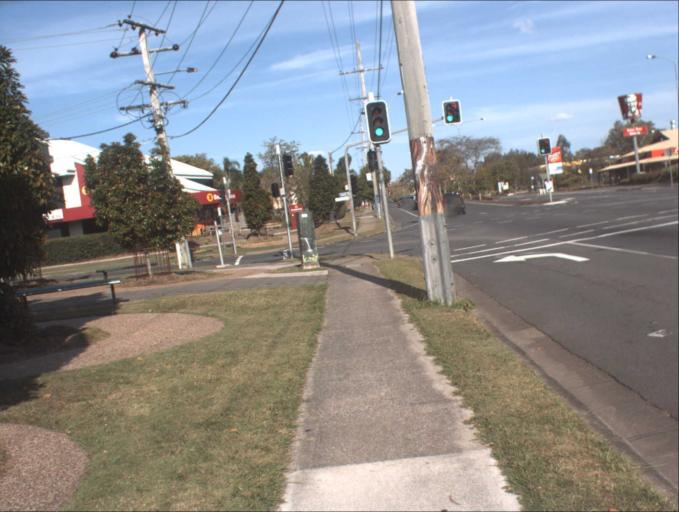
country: AU
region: Queensland
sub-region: Logan
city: Slacks Creek
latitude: -27.6626
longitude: 153.1759
